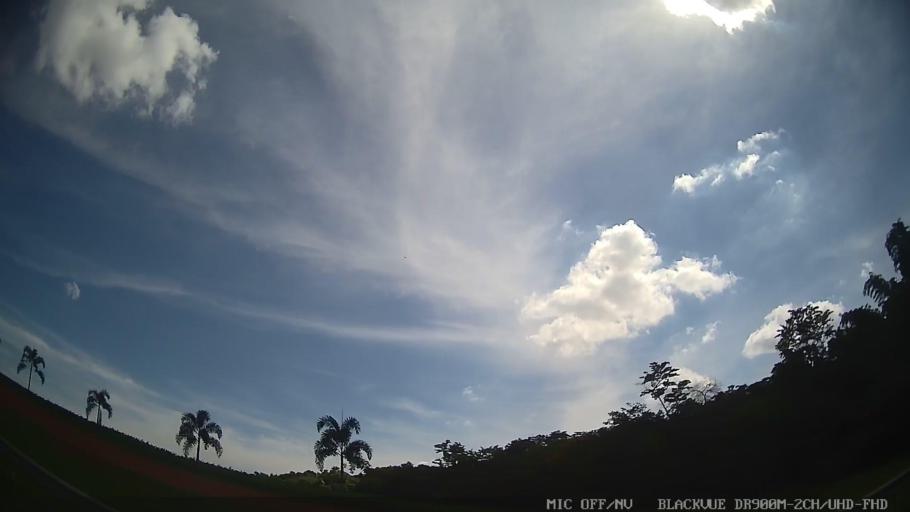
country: BR
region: Sao Paulo
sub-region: Jaguariuna
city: Jaguariuna
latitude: -22.6210
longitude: -47.0632
